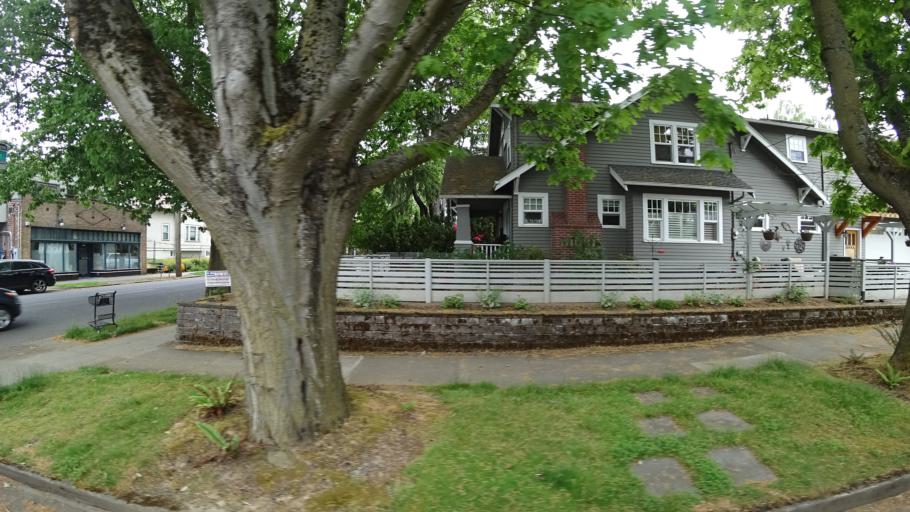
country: US
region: Oregon
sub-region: Multnomah County
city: Portland
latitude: 45.5481
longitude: -122.6544
